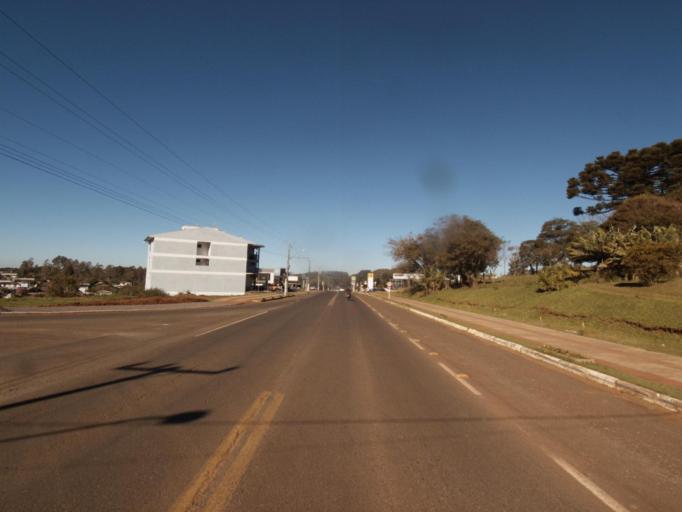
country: AR
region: Misiones
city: Bernardo de Irigoyen
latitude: -26.7499
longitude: -53.5168
